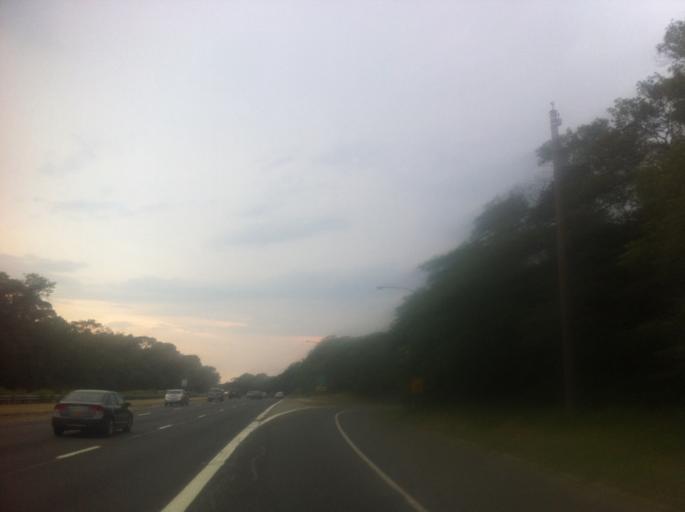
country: US
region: New York
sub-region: Nassau County
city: North Massapequa
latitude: 40.7055
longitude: -73.4466
